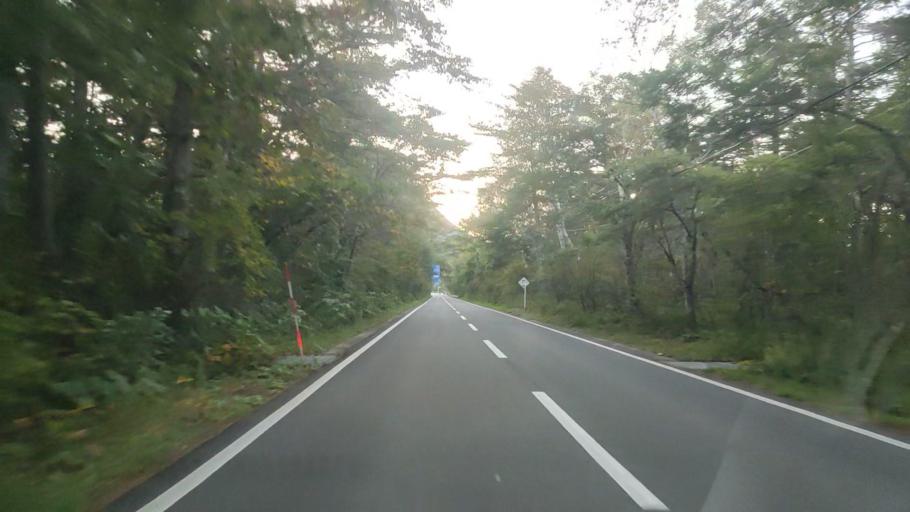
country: JP
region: Nagano
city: Komoro
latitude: 36.4009
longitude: 138.5723
